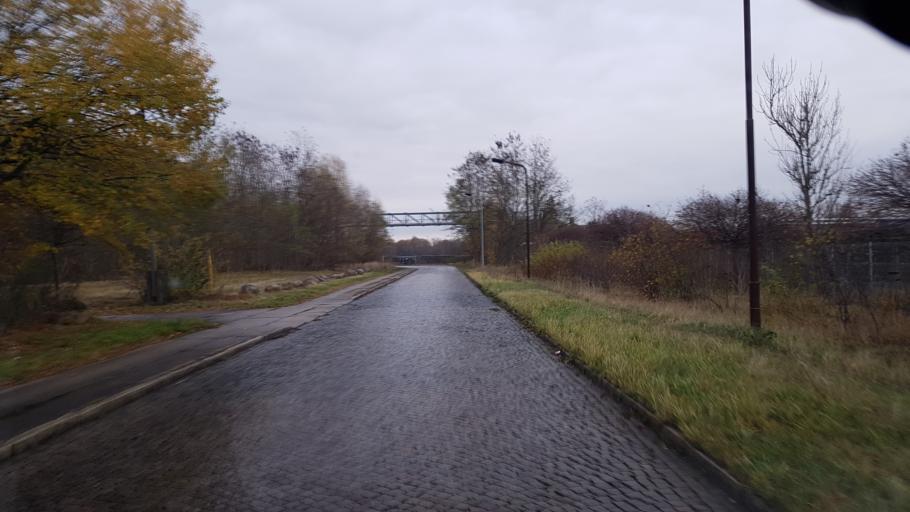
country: DE
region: Brandenburg
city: Lauchhammer
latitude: 51.4917
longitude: 13.7331
